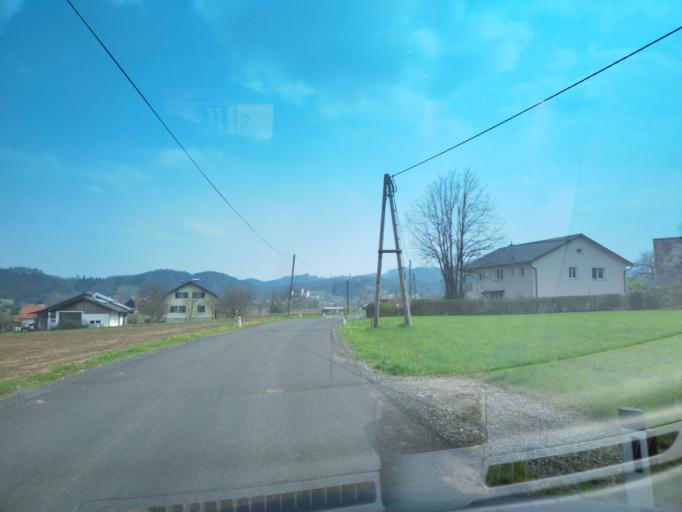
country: AT
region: Styria
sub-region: Politischer Bezirk Leibnitz
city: Grossklein
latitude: 46.7443
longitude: 15.4277
